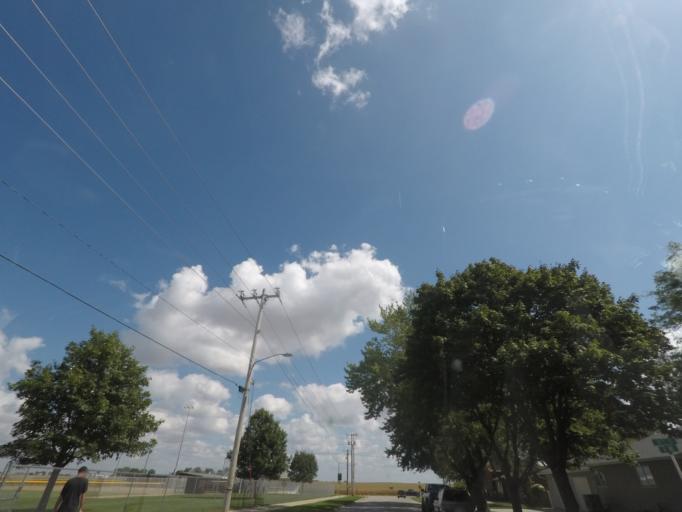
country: US
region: Iowa
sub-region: Story County
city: Nevada
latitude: 42.0191
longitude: -93.4361
